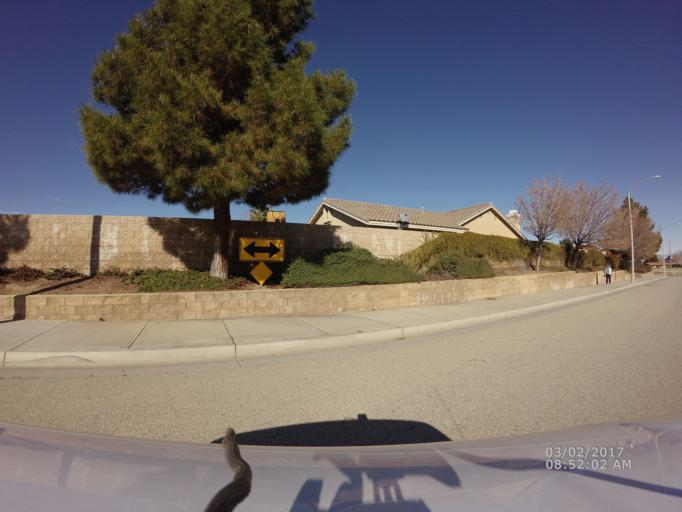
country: US
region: California
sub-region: Los Angeles County
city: Quartz Hill
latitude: 34.6283
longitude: -118.2101
